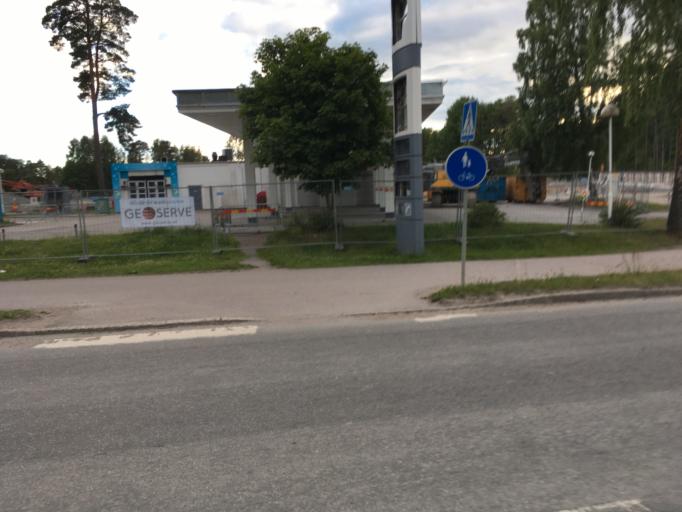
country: SE
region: Uppsala
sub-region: Uppsala Kommun
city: Uppsala
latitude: 59.8391
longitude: 17.6402
